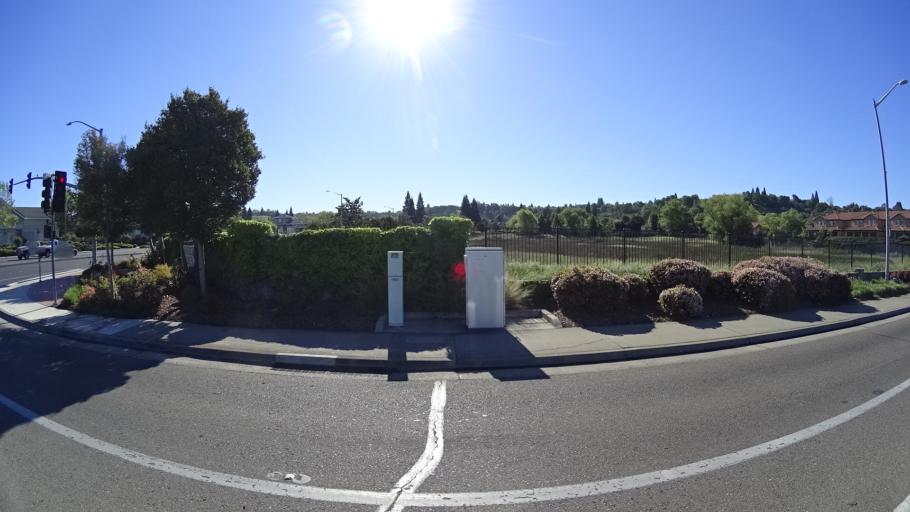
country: US
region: California
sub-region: Placer County
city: Rocklin
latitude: 38.8141
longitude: -121.2580
